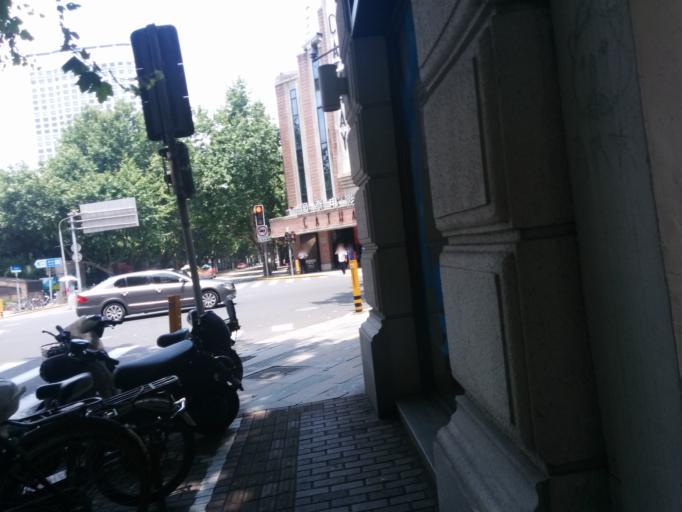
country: CN
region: Shanghai Shi
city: Shanghai
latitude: 31.2194
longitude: 121.4566
